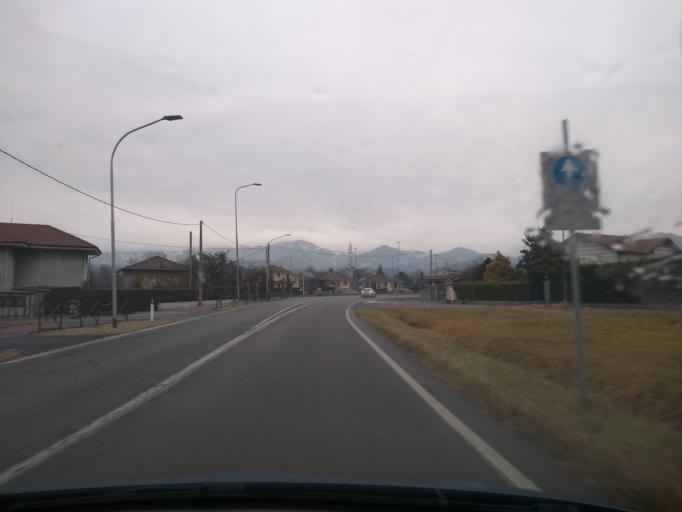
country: IT
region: Piedmont
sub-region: Provincia di Torino
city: Busano
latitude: 45.3333
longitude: 7.6558
